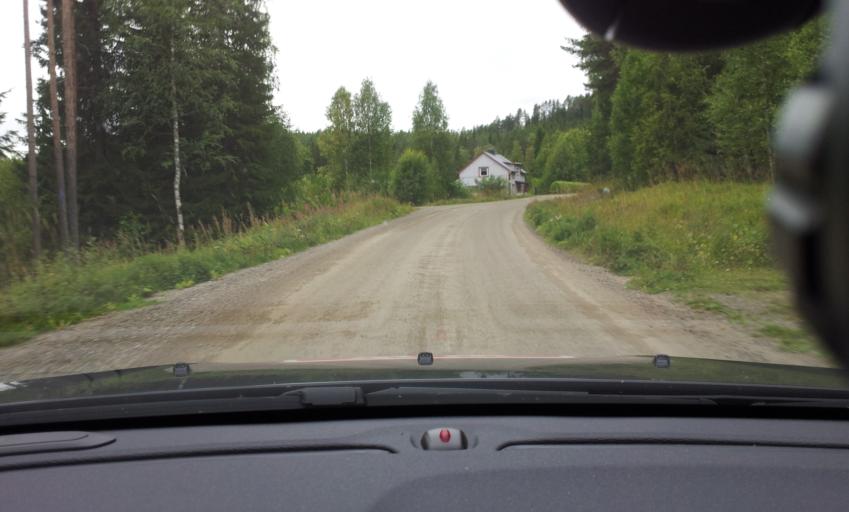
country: SE
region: Jaemtland
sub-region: OEstersunds Kommun
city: Brunflo
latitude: 62.9627
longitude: 15.0130
